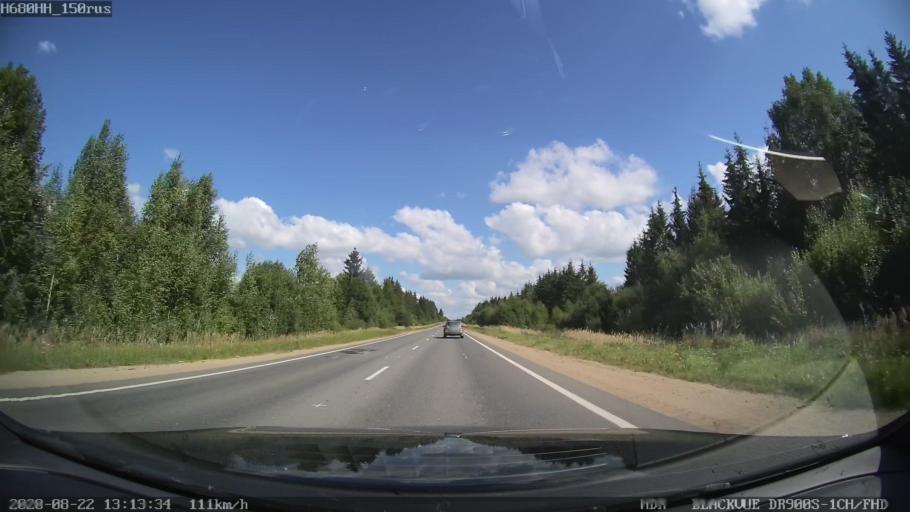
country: RU
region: Tverskaya
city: Bezhetsk
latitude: 57.7510
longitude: 36.5764
